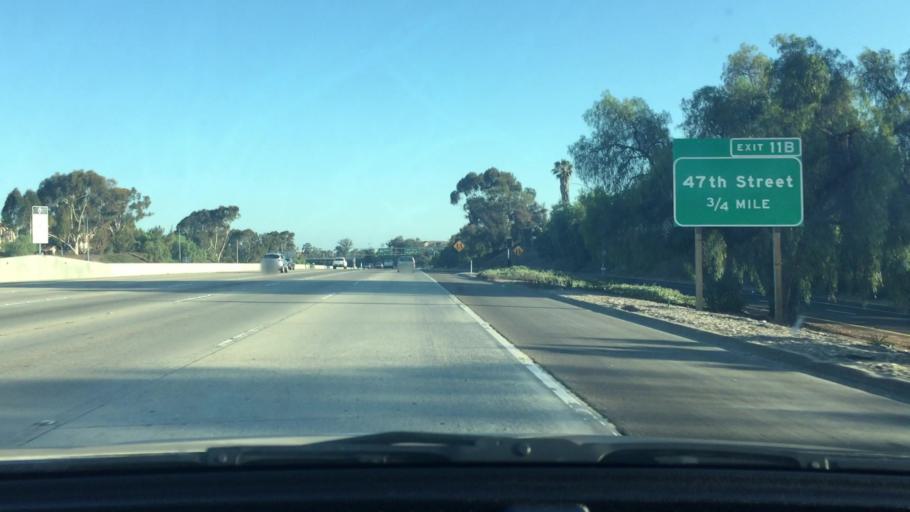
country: US
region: California
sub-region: San Diego County
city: National City
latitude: 32.6783
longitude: -117.0850
